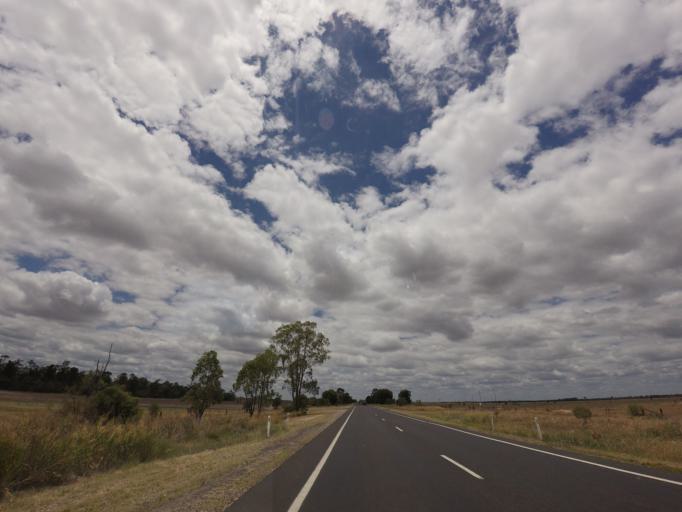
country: AU
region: Queensland
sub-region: Goondiwindi
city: Goondiwindi
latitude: -28.1735
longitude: 150.4926
